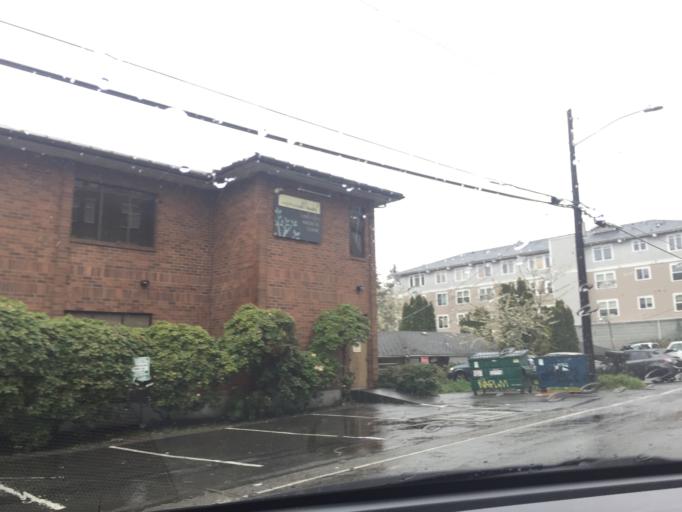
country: US
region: Washington
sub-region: King County
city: Lake Forest Park
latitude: 47.7219
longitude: -122.2964
